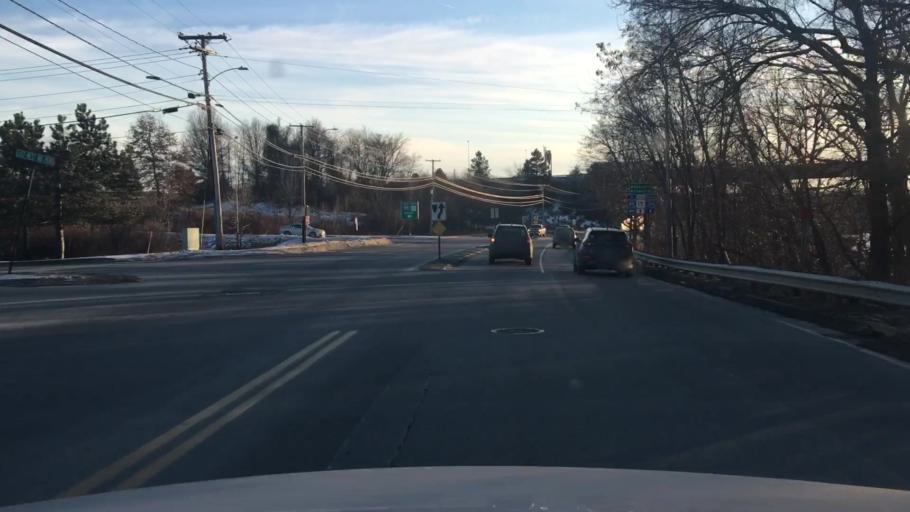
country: US
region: Maine
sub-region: Penobscot County
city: Brewer
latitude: 44.7864
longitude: -68.7709
